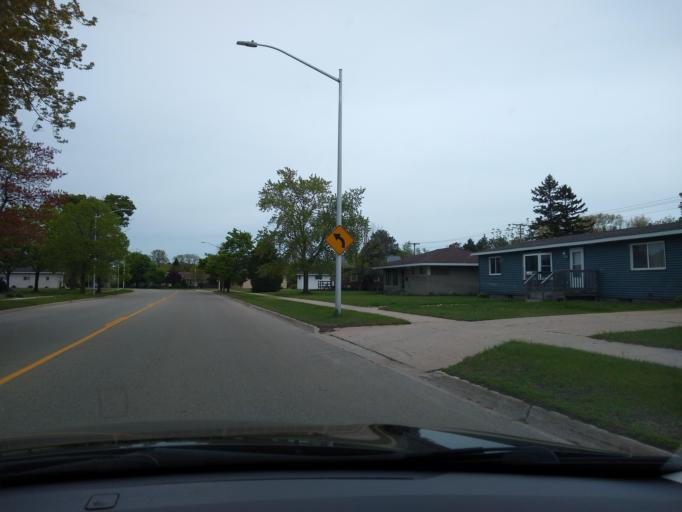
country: US
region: Michigan
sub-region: Delta County
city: Escanaba
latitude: 45.7599
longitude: -87.0696
